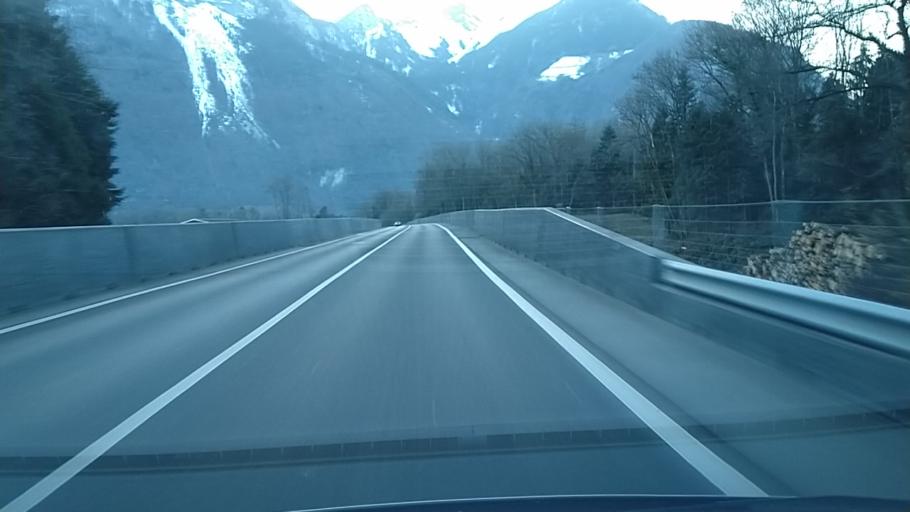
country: CH
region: Valais
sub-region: Monthey District
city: Vouvry
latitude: 46.3588
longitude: 6.8974
